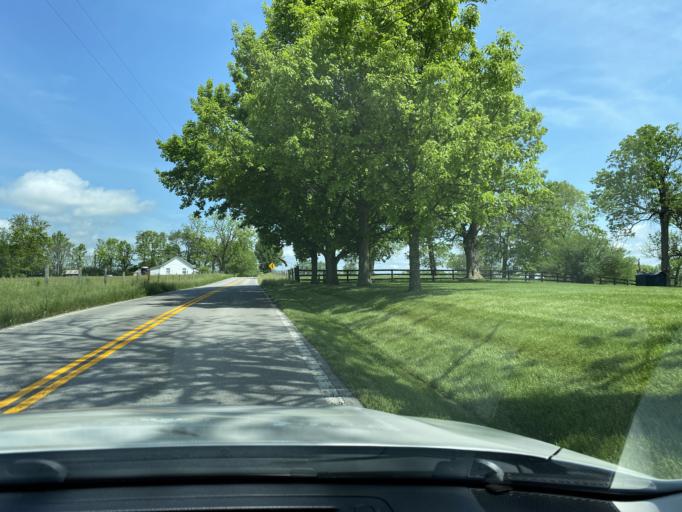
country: US
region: Kentucky
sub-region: Scott County
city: Georgetown
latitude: 38.2512
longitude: -84.5893
